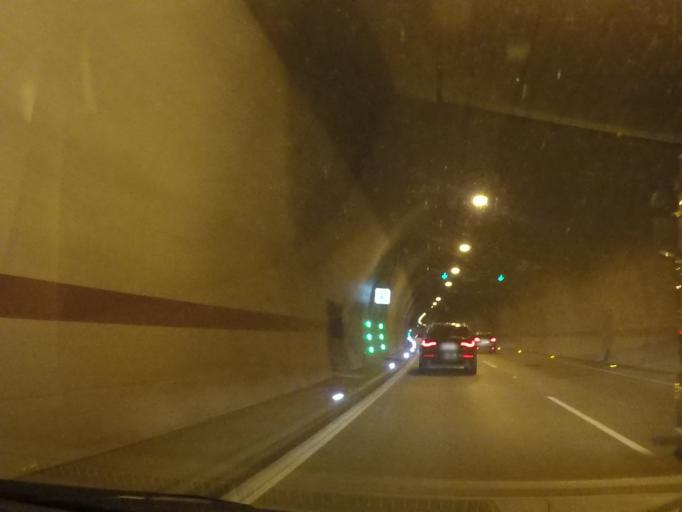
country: SK
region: Bratislavsky
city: Bratislava
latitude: 48.1651
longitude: 17.0727
